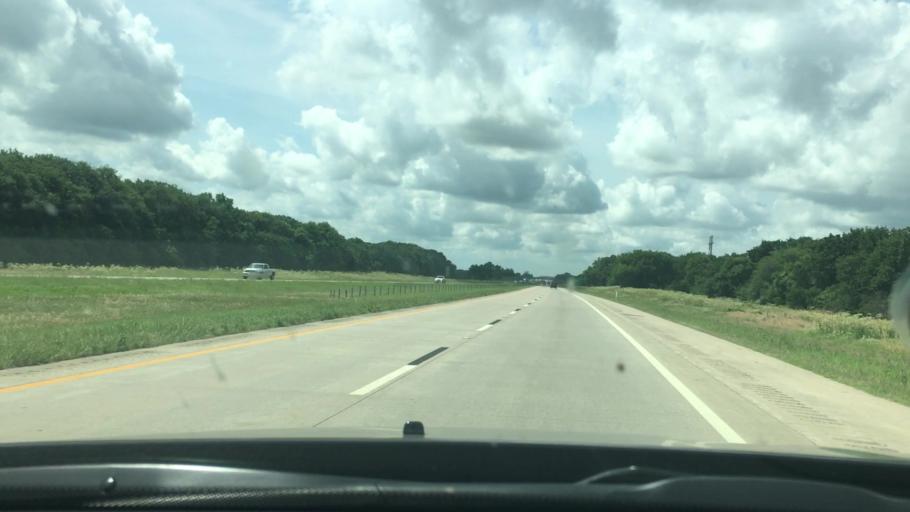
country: US
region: Oklahoma
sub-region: Love County
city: Marietta
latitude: 33.8050
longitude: -97.1351
